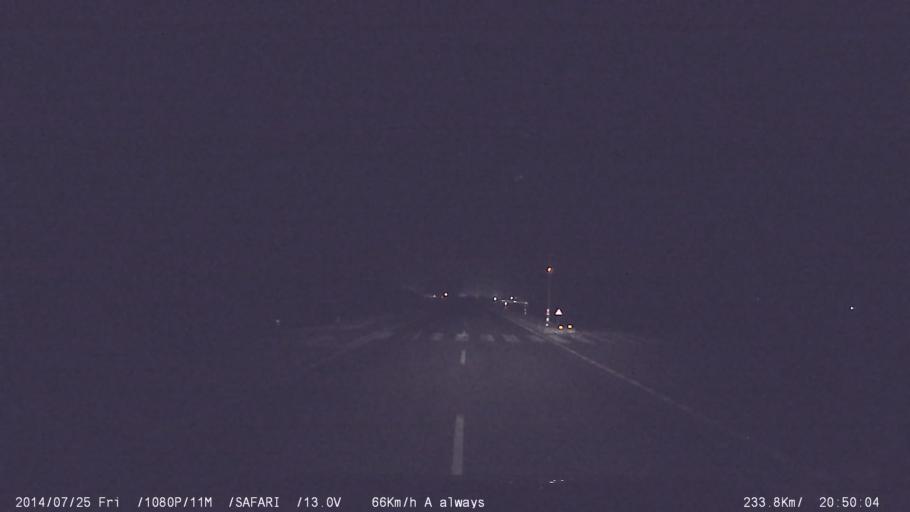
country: IN
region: Tamil Nadu
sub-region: Salem
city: Idappadi
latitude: 11.4903
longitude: 77.8516
